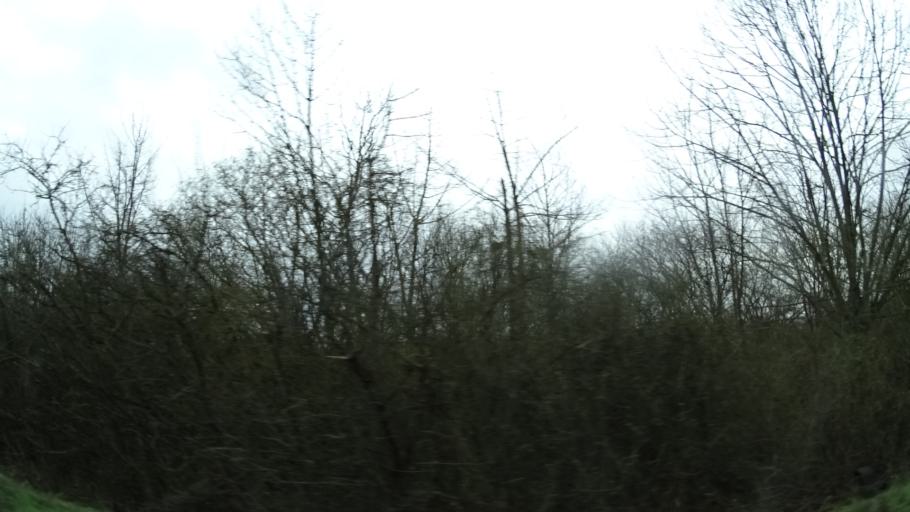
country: DE
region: Hesse
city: Gernsheim
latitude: 49.7610
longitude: 8.5027
